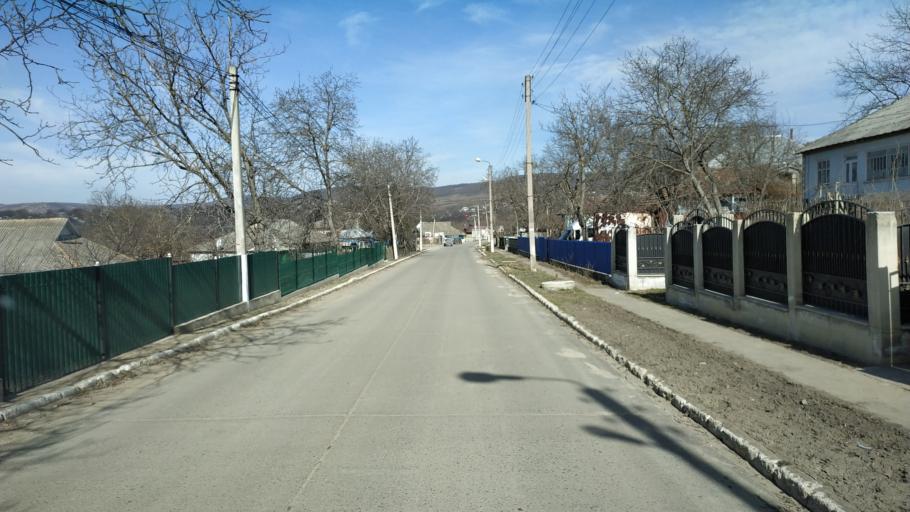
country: MD
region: Nisporeni
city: Nisporeni
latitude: 47.0741
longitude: 28.2608
